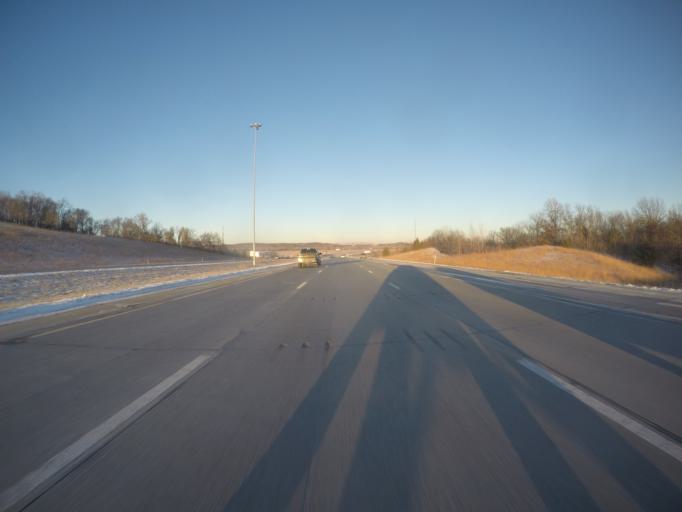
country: US
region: Missouri
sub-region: Platte County
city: Parkville
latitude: 39.1816
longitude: -94.7961
